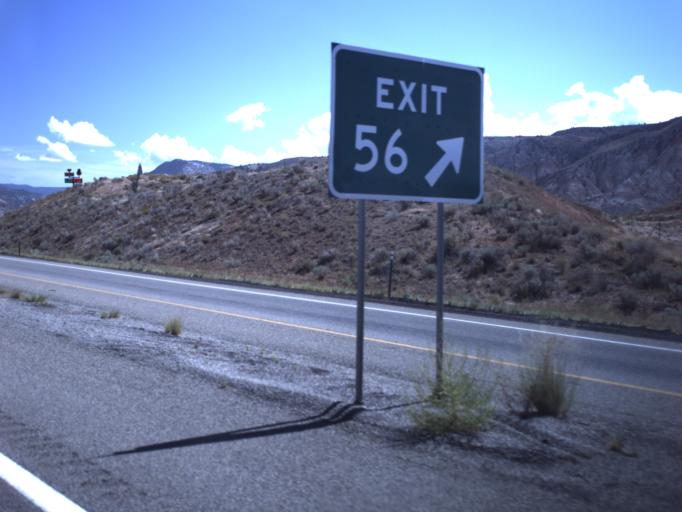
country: US
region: Utah
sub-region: Sevier County
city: Salina
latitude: 38.9330
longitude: -111.8600
